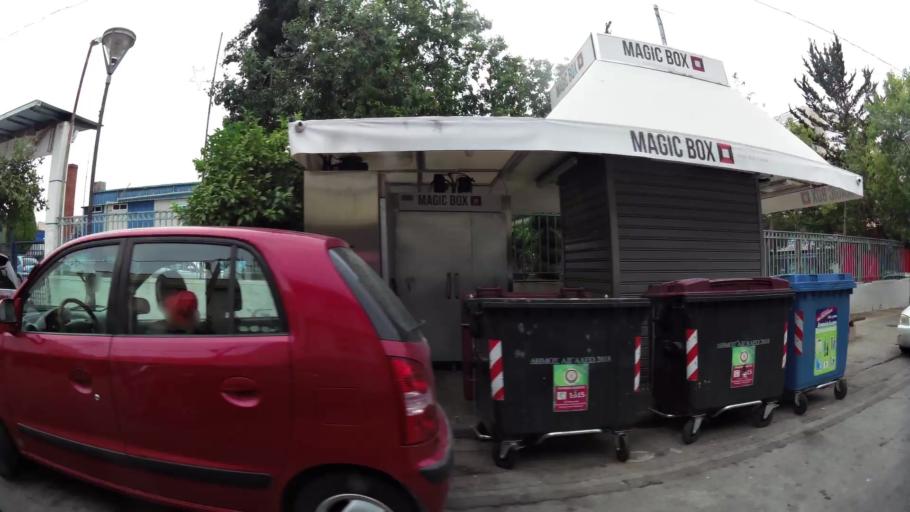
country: GR
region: Attica
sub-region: Nomarchia Athinas
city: Aigaleo
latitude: 37.9945
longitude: 23.6825
